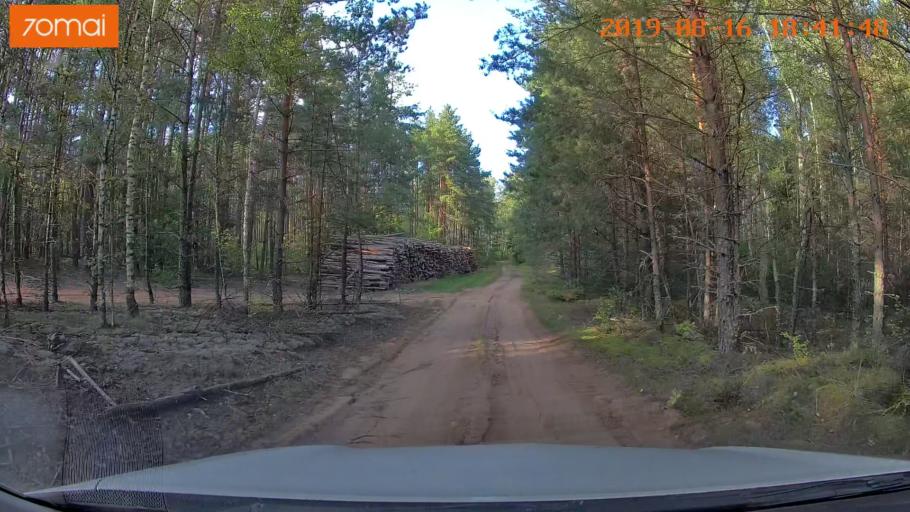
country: BY
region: Mogilev
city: Asipovichy
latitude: 53.2134
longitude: 28.6455
